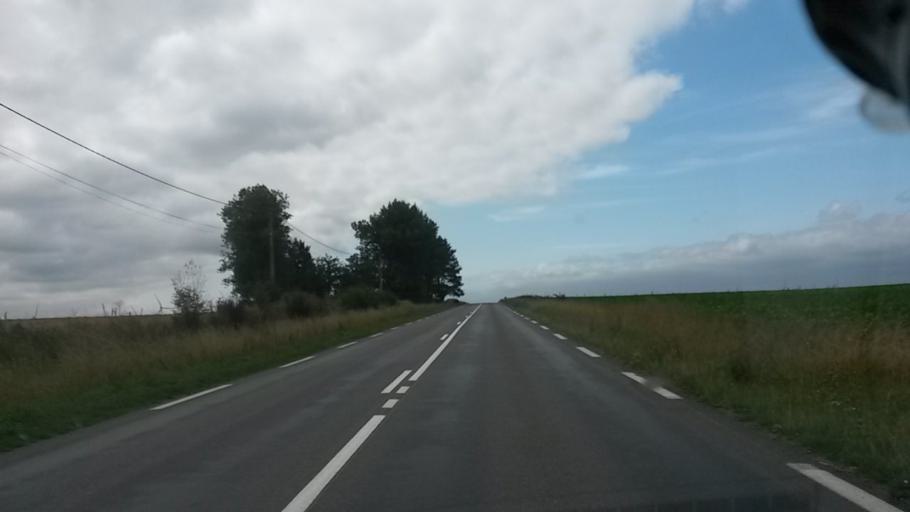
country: FR
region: Nord-Pas-de-Calais
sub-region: Departement du Pas-de-Calais
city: Bourlon
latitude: 50.1529
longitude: 3.0943
